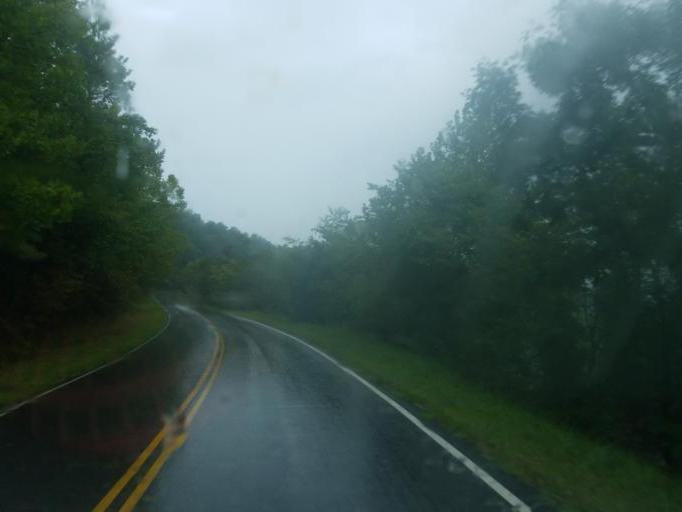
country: US
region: Kentucky
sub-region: Carter County
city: Grayson
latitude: 38.4915
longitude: -82.9872
